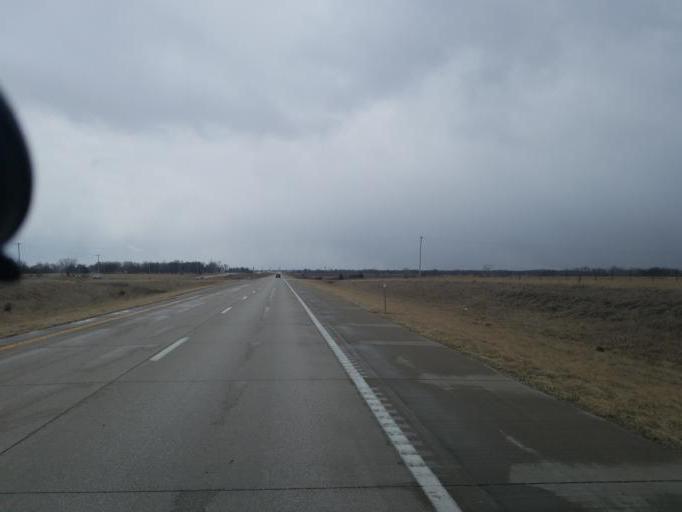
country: US
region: Missouri
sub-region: Randolph County
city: Moberly
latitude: 39.4843
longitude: -92.4345
